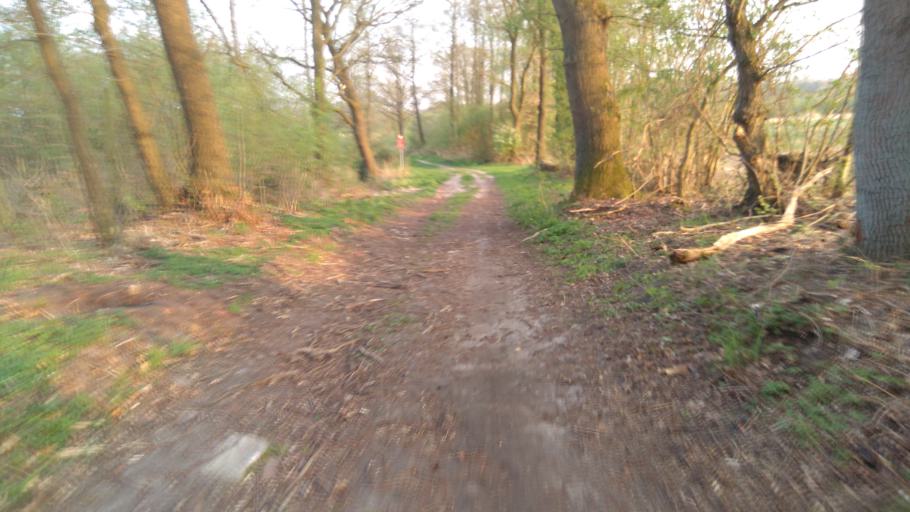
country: DE
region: Lower Saxony
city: Bliedersdorf
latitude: 53.4936
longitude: 9.5543
